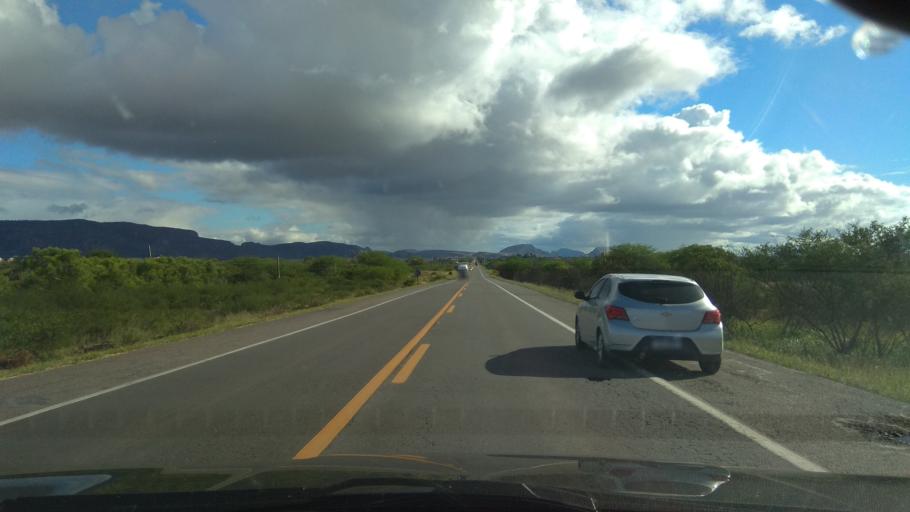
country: BR
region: Bahia
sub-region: Castro Alves
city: Castro Alves
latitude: -12.6894
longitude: -39.6893
